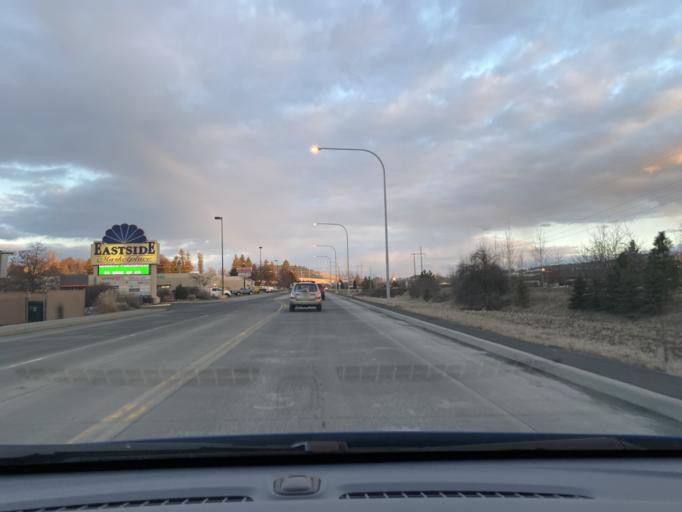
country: US
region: Idaho
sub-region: Latah County
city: Moscow
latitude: 46.7211
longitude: -116.9858
